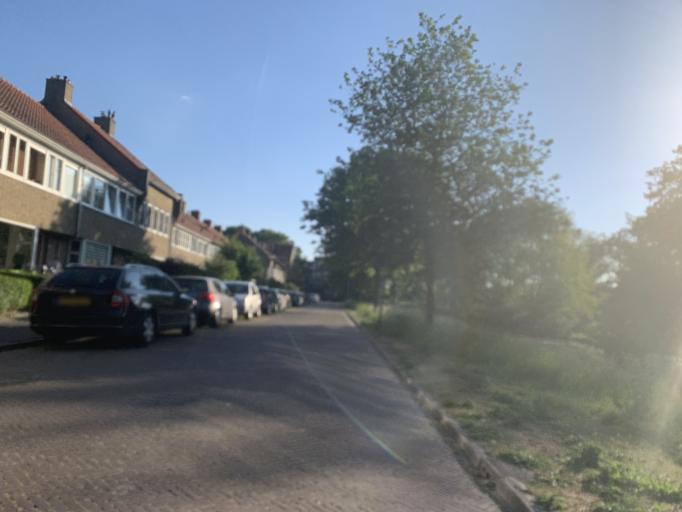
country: NL
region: Groningen
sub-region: Gemeente Groningen
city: Oosterpark
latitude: 53.2026
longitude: 6.5834
